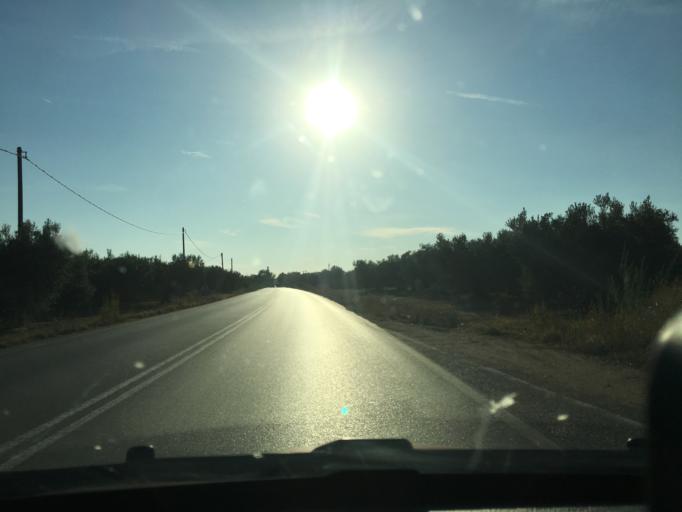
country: GR
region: Central Macedonia
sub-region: Nomos Chalkidikis
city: Olynthos
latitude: 40.2828
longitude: 23.3613
